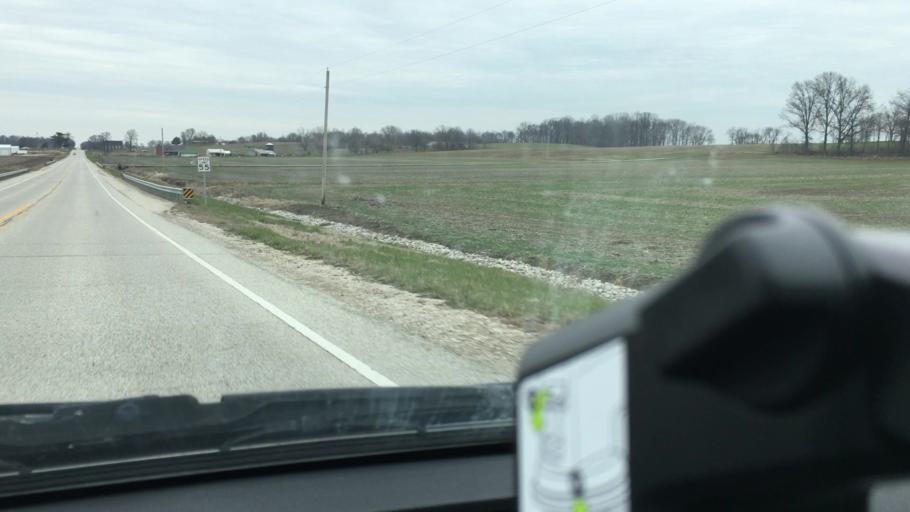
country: US
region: Indiana
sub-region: Greene County
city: Bloomfield
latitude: 38.9686
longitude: -87.0167
